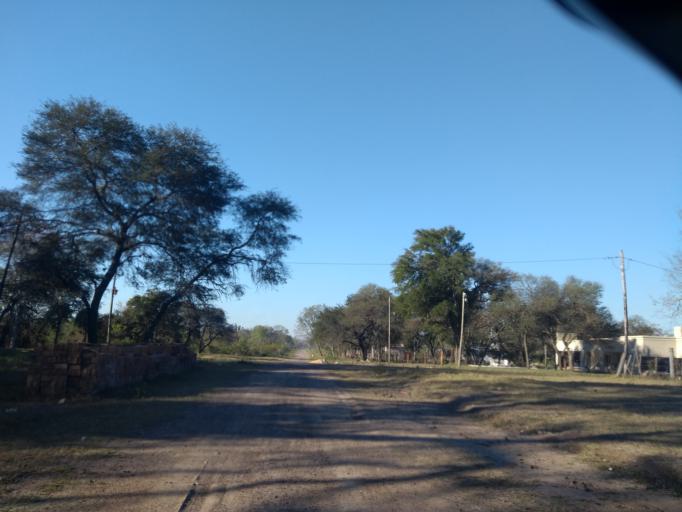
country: AR
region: Chaco
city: Barranqueras
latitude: -27.4385
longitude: -58.9296
